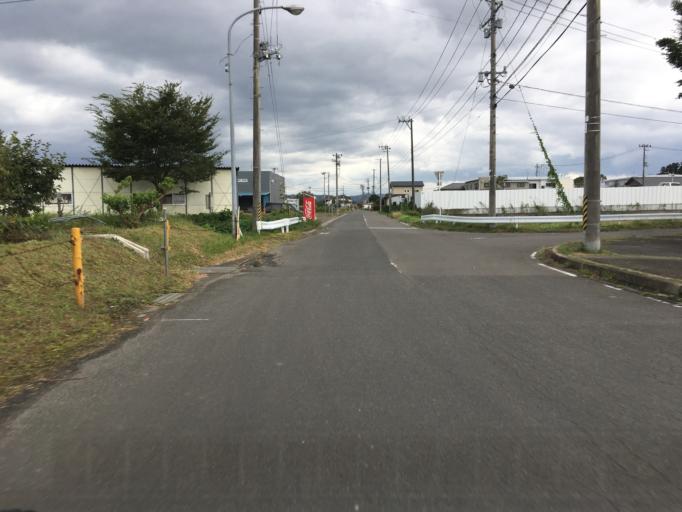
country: JP
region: Fukushima
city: Yanagawamachi-saiwaicho
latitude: 37.8579
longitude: 140.5961
